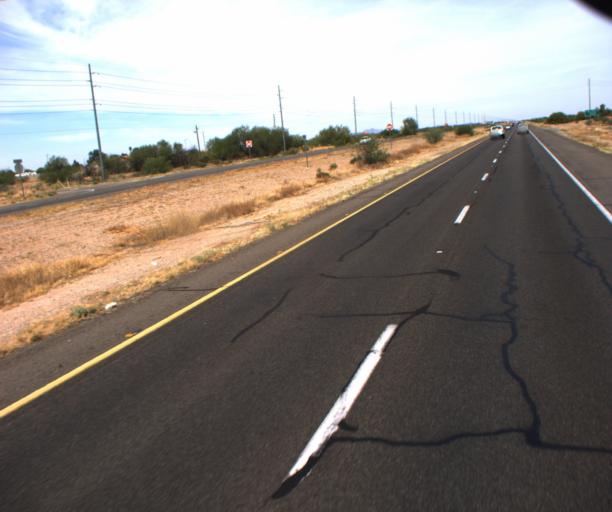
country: US
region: Arizona
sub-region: Maricopa County
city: Sun City West
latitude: 33.7105
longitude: -112.4421
